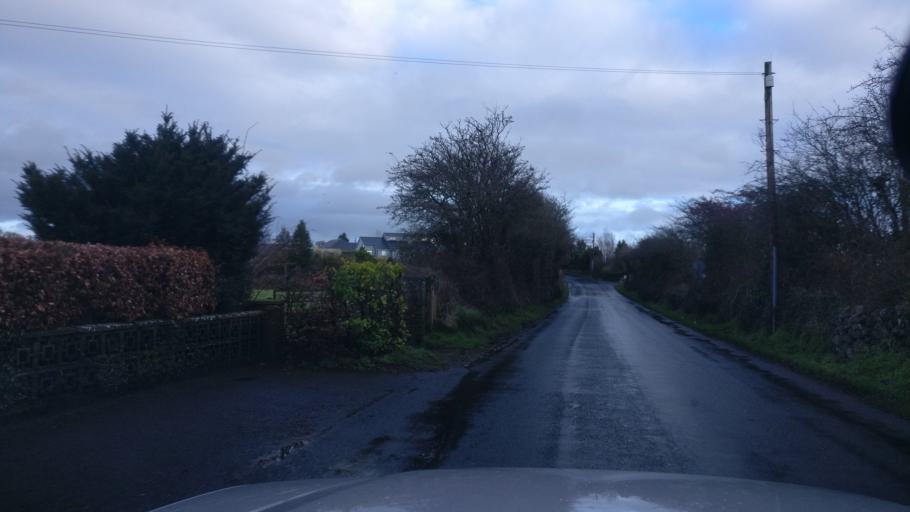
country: IE
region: Connaught
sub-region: County Galway
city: Athenry
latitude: 53.2988
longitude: -8.7388
